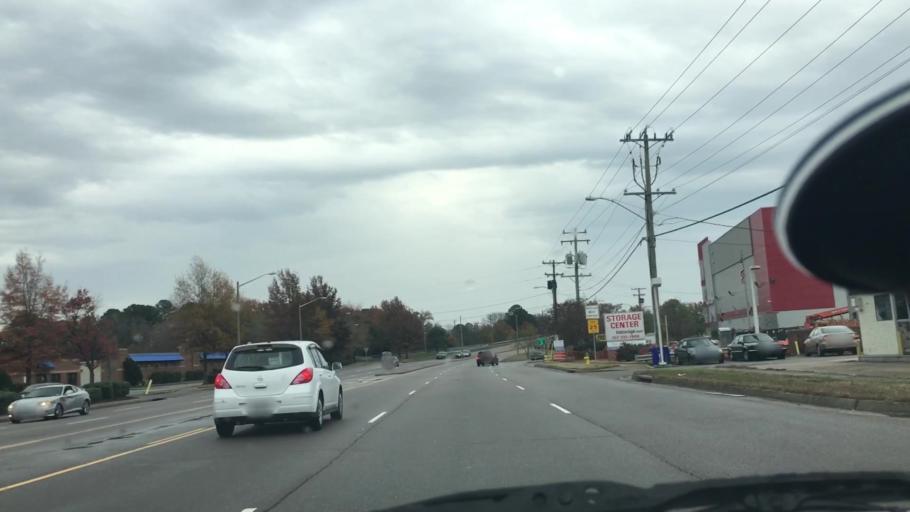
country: US
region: Virginia
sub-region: City of Norfolk
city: Norfolk
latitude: 36.9009
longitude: -76.2564
